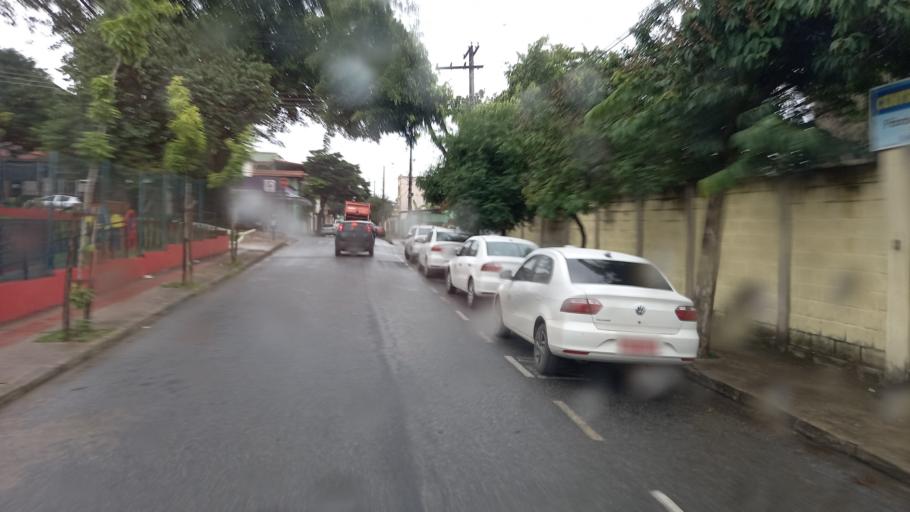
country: BR
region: Minas Gerais
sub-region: Belo Horizonte
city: Belo Horizonte
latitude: -19.8667
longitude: -43.9249
